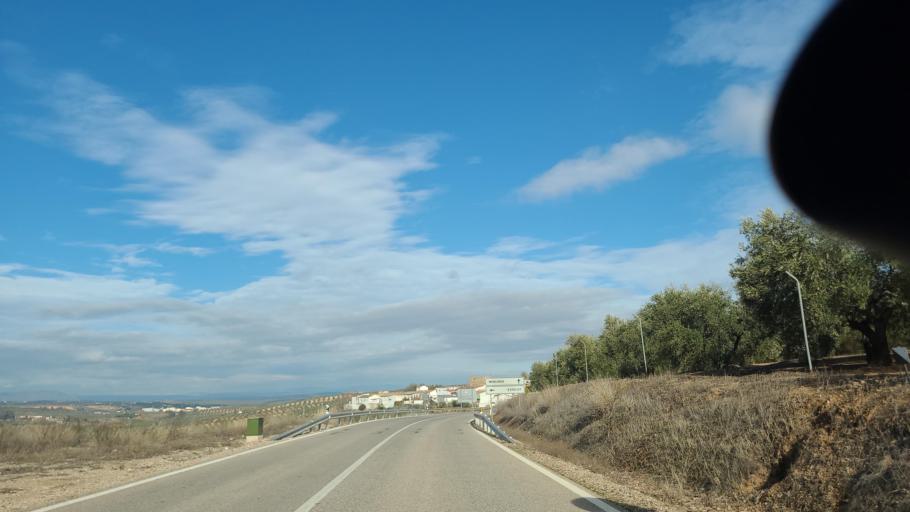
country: ES
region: Andalusia
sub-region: Provincia de Jaen
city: Espeluy
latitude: 38.0299
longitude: -3.8654
